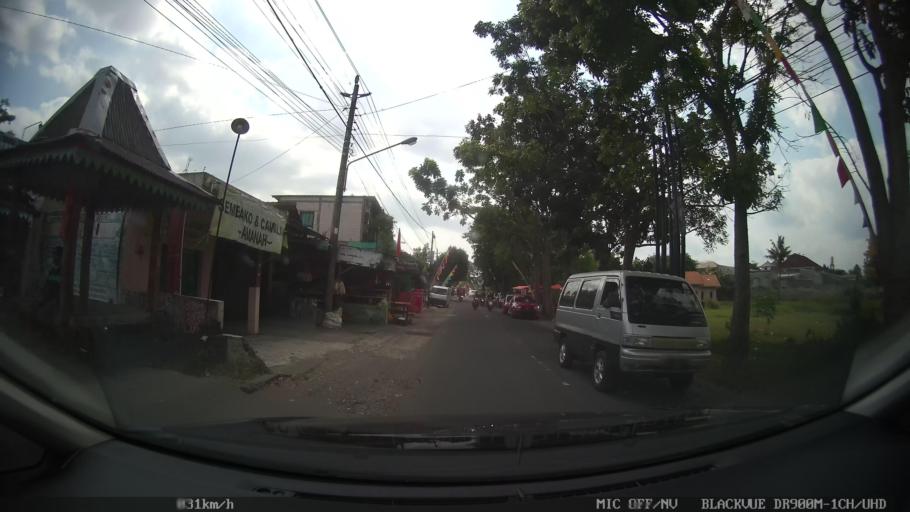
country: ID
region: Daerah Istimewa Yogyakarta
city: Yogyakarta
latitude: -7.7640
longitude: 110.3484
